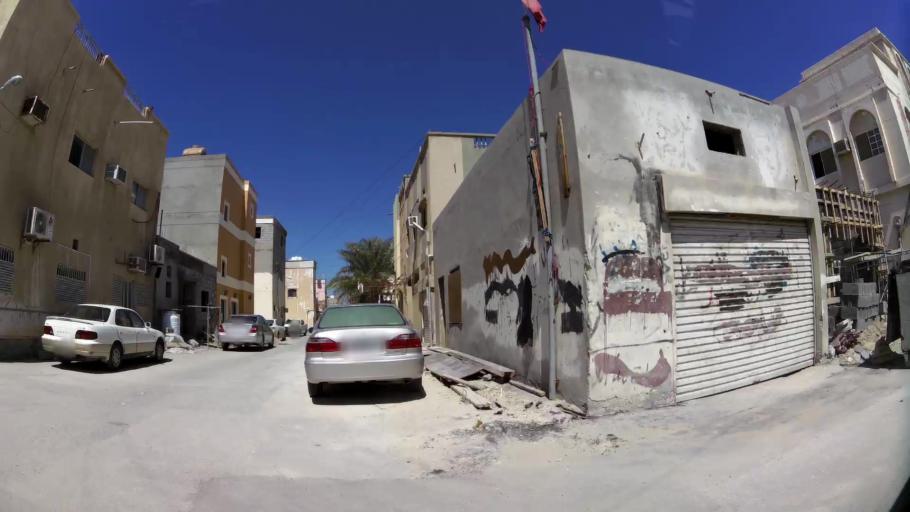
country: BH
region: Muharraq
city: Al Muharraq
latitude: 26.2853
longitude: 50.6266
